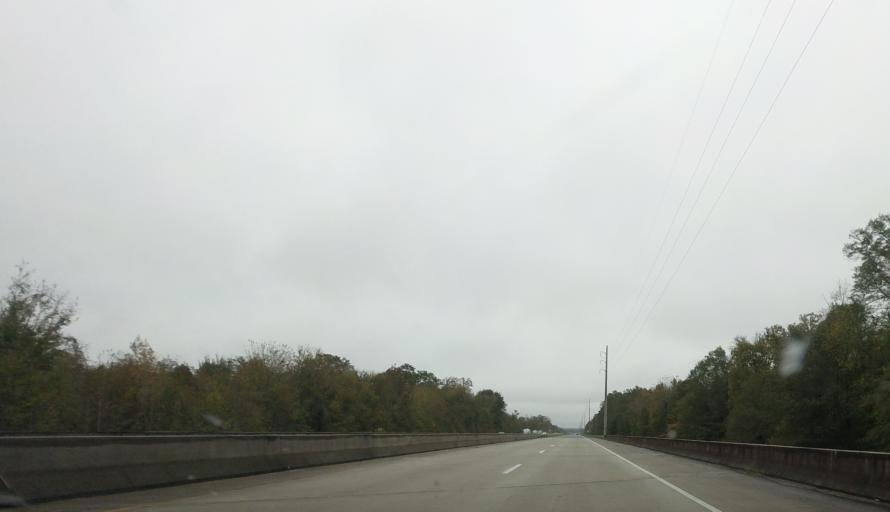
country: US
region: Georgia
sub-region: Taylor County
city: Reynolds
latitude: 32.5501
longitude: -84.0474
